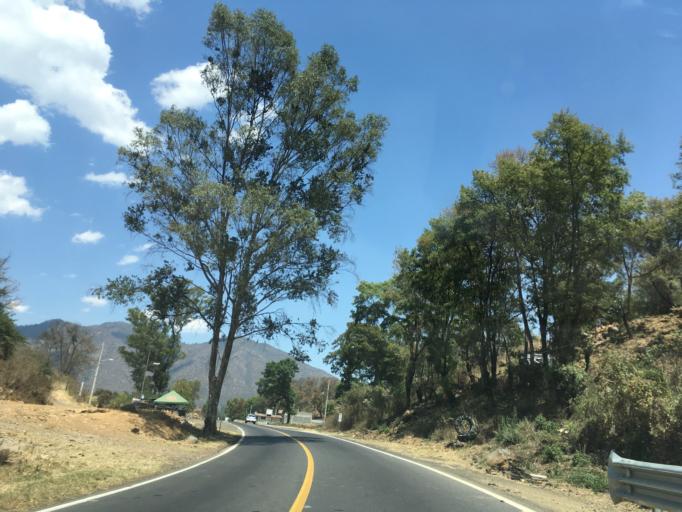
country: MX
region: Michoacan
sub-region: Chilchota
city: Tacuro (Santa Maria Tacuro)
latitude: 19.8438
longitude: -102.0308
